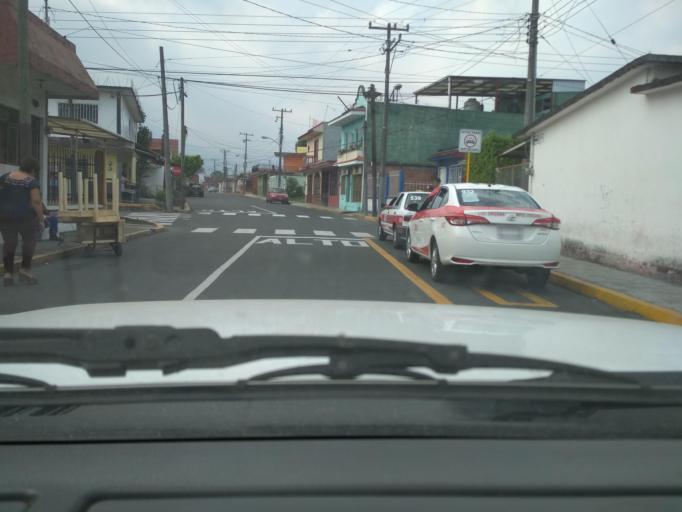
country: MX
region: Veracruz
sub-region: Mariano Escobedo
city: Palmira
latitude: 18.8715
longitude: -97.0993
